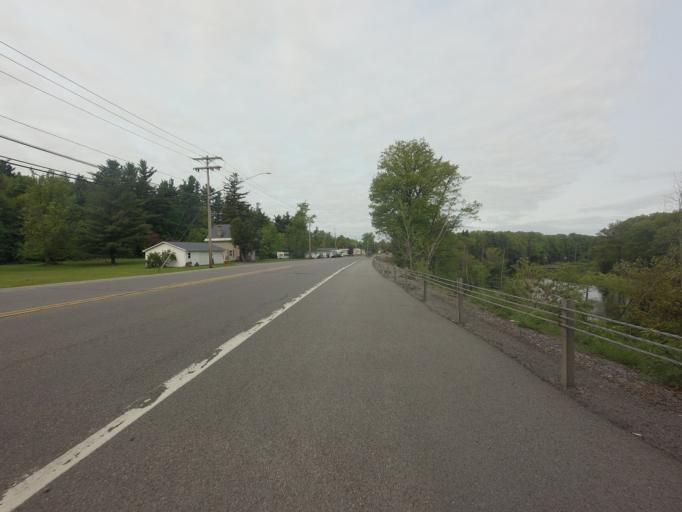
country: US
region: New York
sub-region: Jefferson County
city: Black River
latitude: 44.0061
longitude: -75.7872
